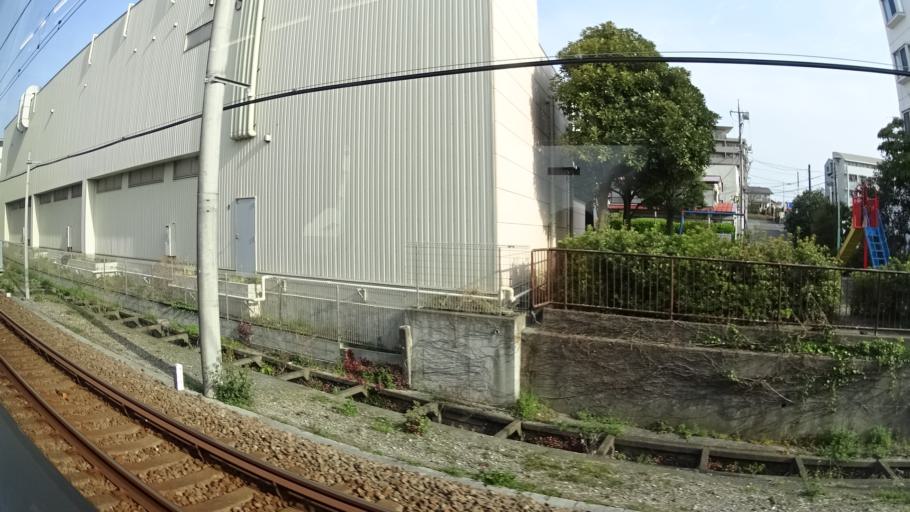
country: JP
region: Kanagawa
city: Minami-rinkan
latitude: 35.4598
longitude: 139.5159
